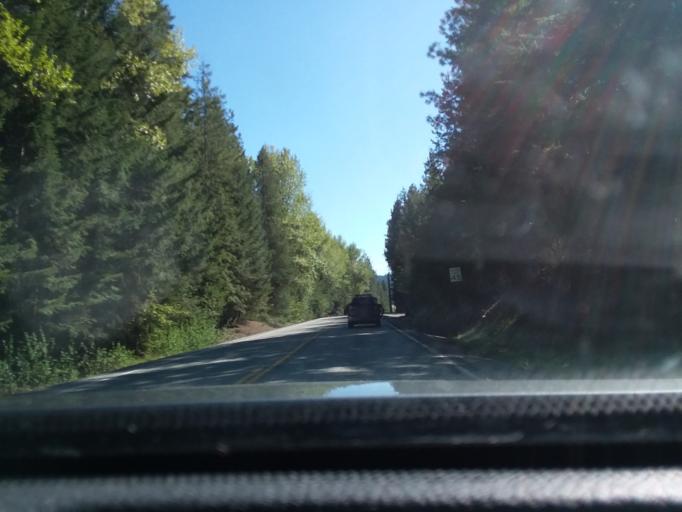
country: US
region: Washington
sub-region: Chelan County
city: Leavenworth
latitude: 47.7858
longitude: -120.6652
